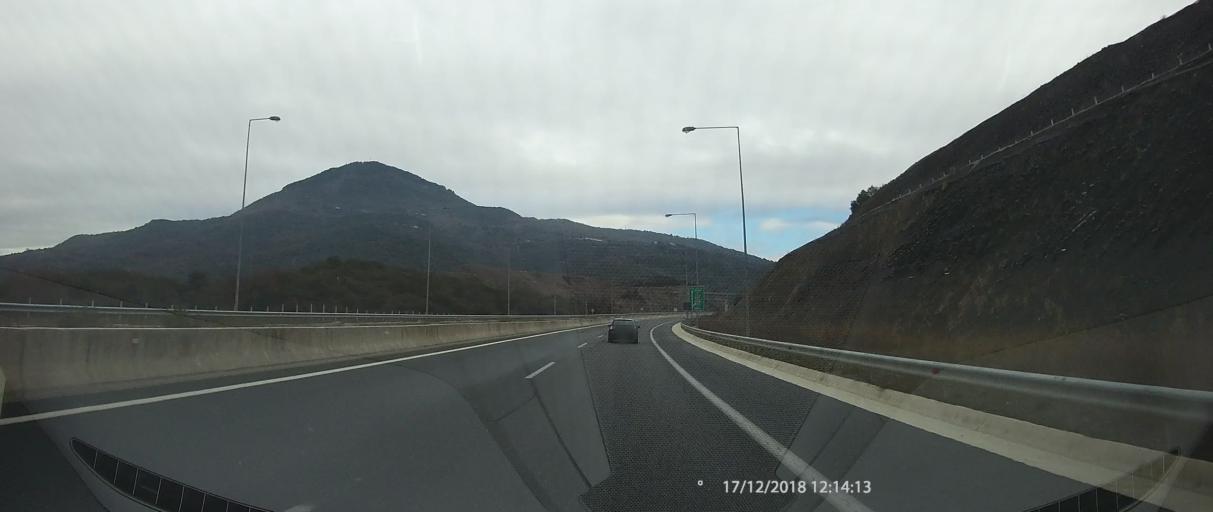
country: GR
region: Epirus
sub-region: Nomos Ioanninon
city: Katsikas
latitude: 39.7165
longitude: 20.9912
